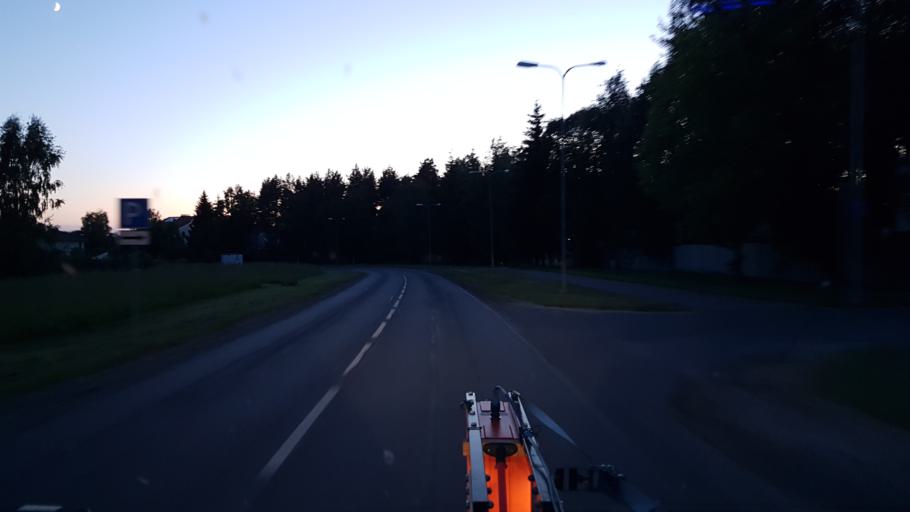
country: EE
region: Harju
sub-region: Harku vald
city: Tabasalu
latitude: 59.4361
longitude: 24.6114
